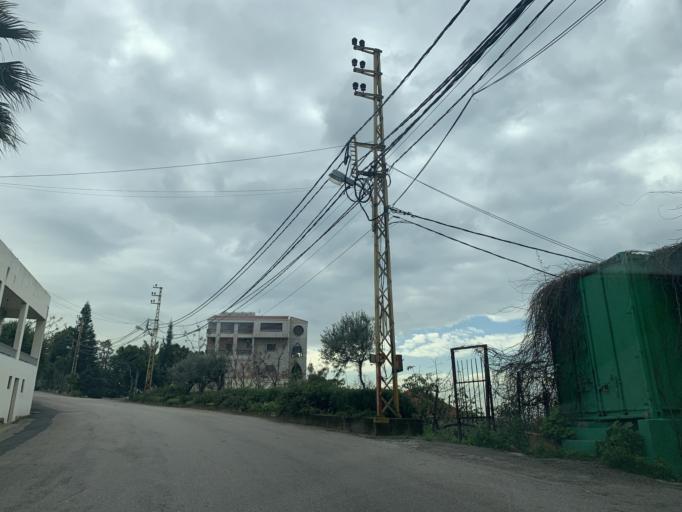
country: LB
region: Mont-Liban
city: Djounie
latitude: 34.0455
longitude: 35.6357
